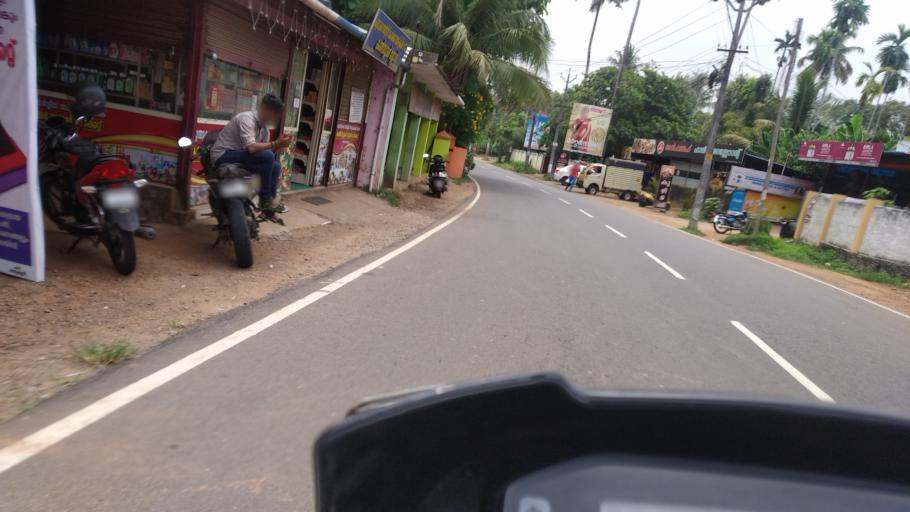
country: IN
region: Kerala
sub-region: Ernakulam
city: Aluva
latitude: 10.1560
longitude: 76.3202
